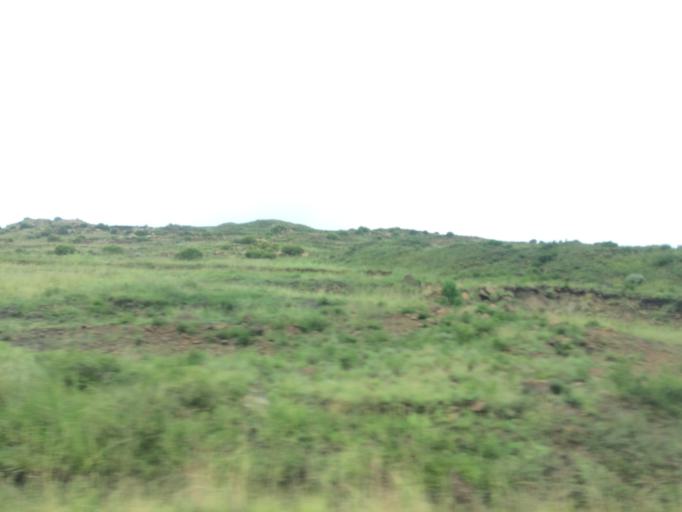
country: LS
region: Maseru
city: Nako
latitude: -29.7576
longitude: 27.5184
